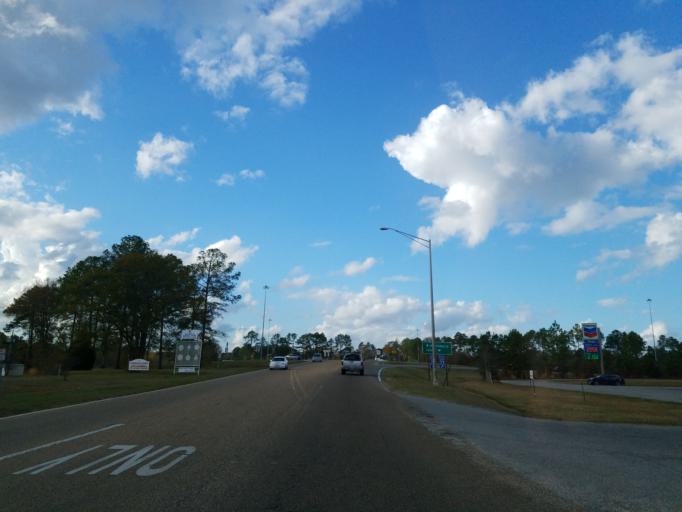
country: US
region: Mississippi
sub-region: Jones County
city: Ellisville
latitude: 31.6113
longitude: -89.2057
